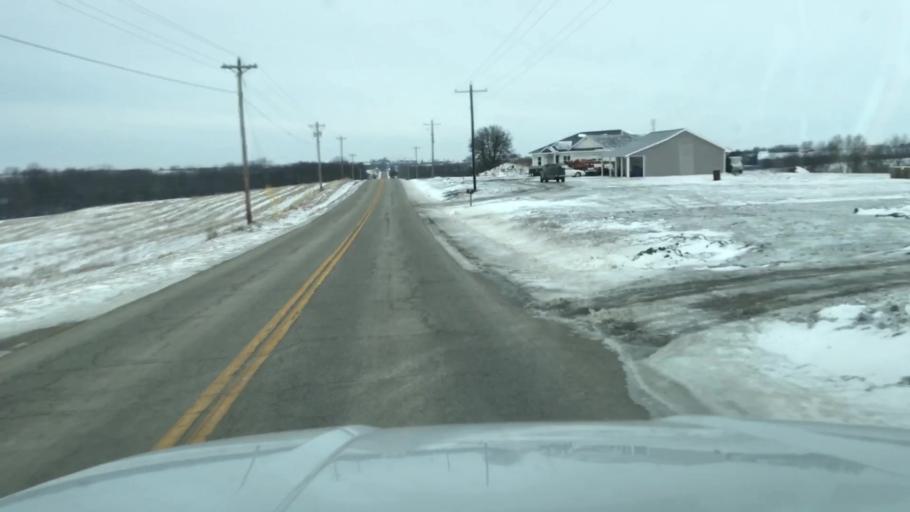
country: US
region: Missouri
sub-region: Andrew County
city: Savannah
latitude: 40.0248
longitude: -94.8847
